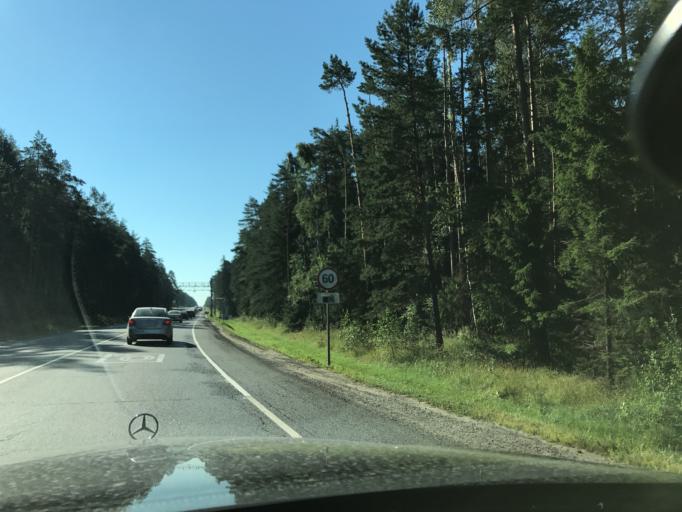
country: RU
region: Moskovskaya
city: Noginsk-9
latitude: 56.0981
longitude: 38.6692
